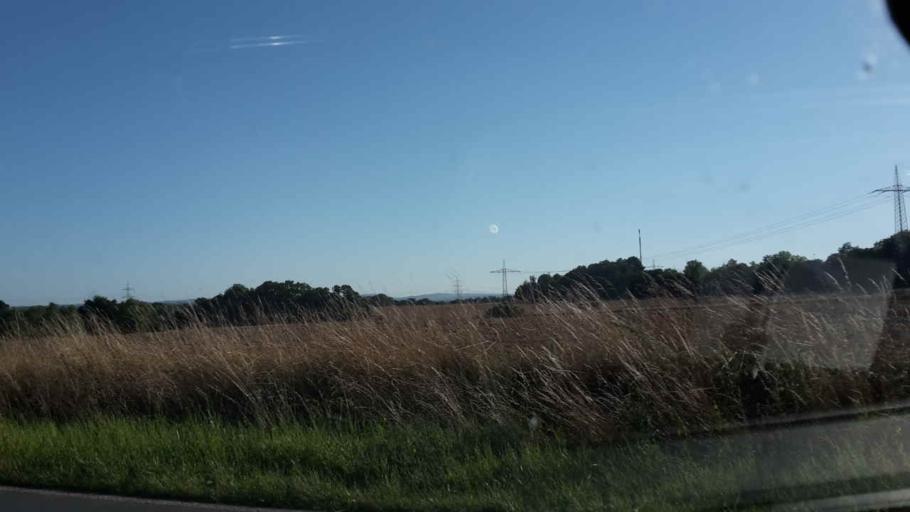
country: DE
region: North Rhine-Westphalia
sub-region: Regierungsbezirk Arnsberg
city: Holzwickede
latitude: 51.4703
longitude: 7.6029
